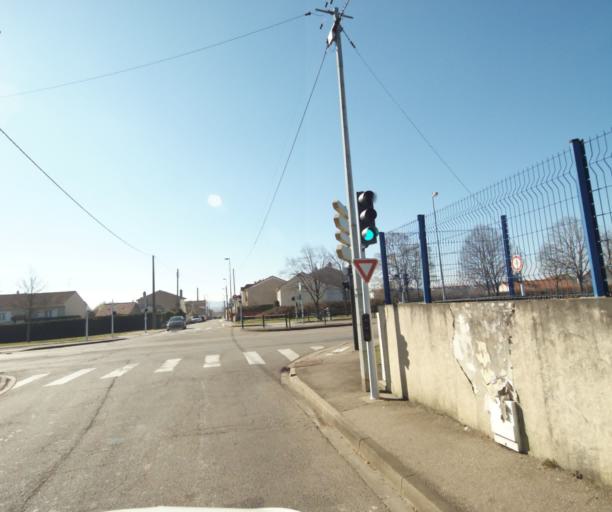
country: FR
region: Lorraine
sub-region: Departement de Meurthe-et-Moselle
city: Tomblaine
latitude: 48.6864
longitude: 6.2182
